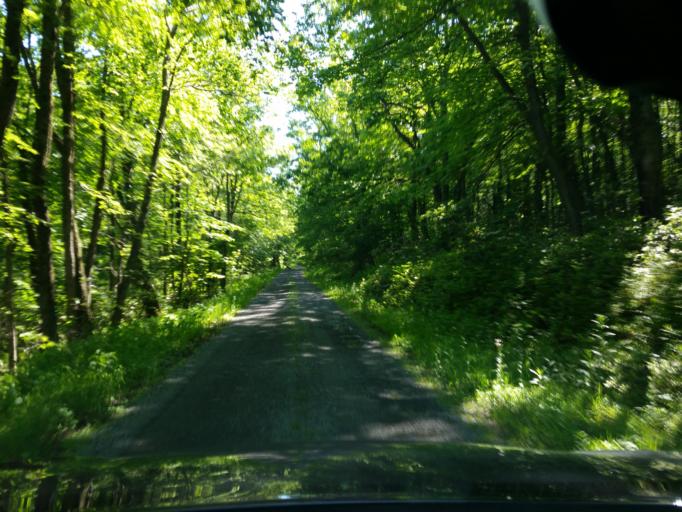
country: US
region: Pennsylvania
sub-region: Lycoming County
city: Duboistown
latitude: 41.1273
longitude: -77.0997
